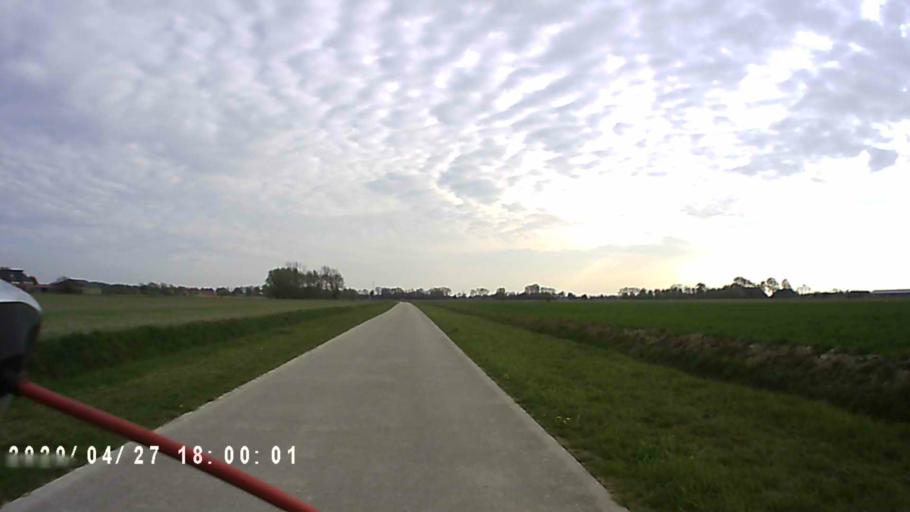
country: NL
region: Groningen
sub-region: Gemeente Winsum
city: Winsum
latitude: 53.4094
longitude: 6.4539
